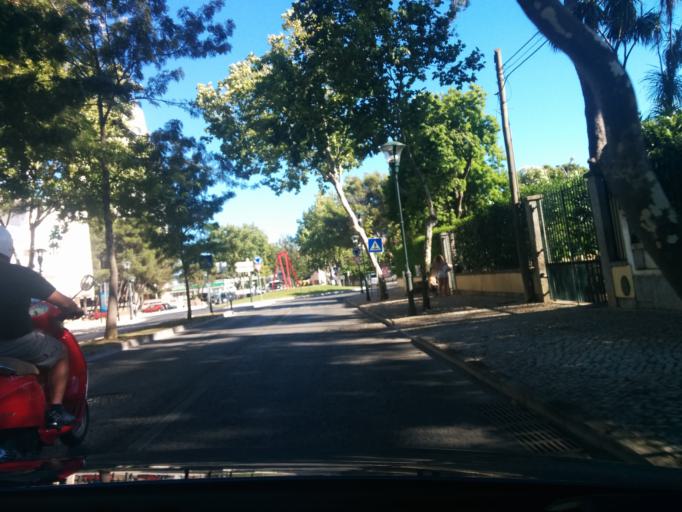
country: PT
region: Lisbon
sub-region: Cascais
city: Cascais
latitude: 38.6980
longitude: -9.4317
